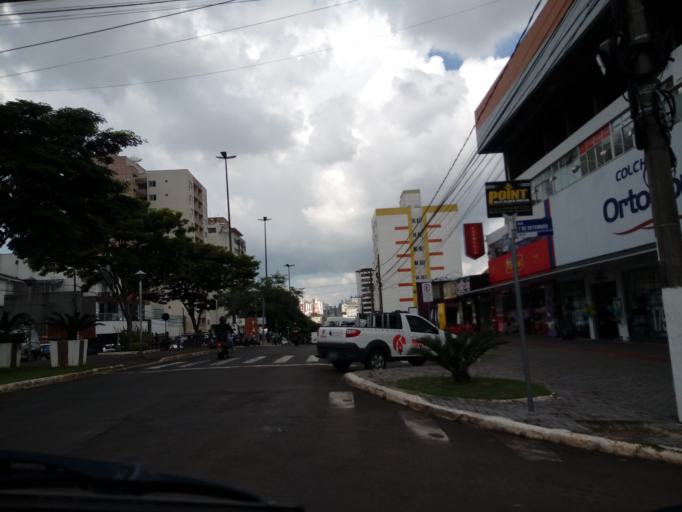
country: BR
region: Santa Catarina
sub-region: Chapeco
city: Chapeco
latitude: -27.0953
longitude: -52.6170
